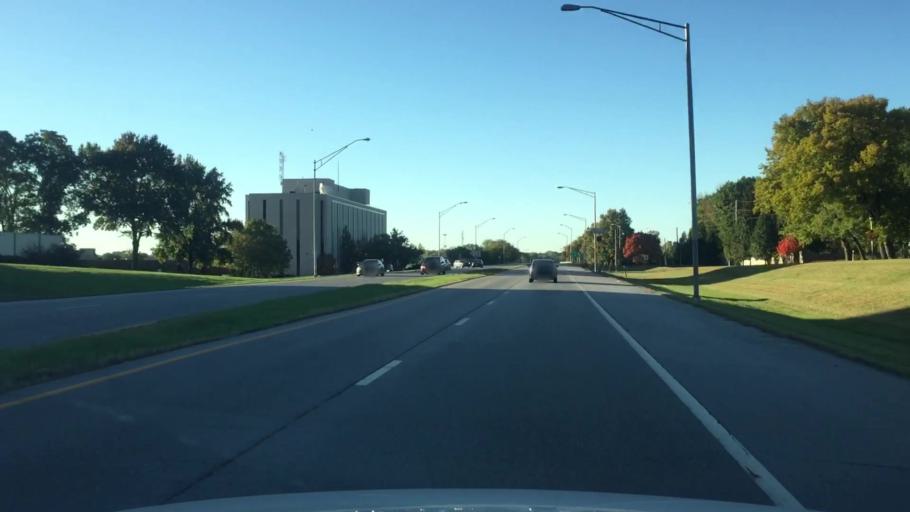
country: US
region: Kansas
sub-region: Johnson County
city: Mission
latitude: 39.0258
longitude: -94.6680
